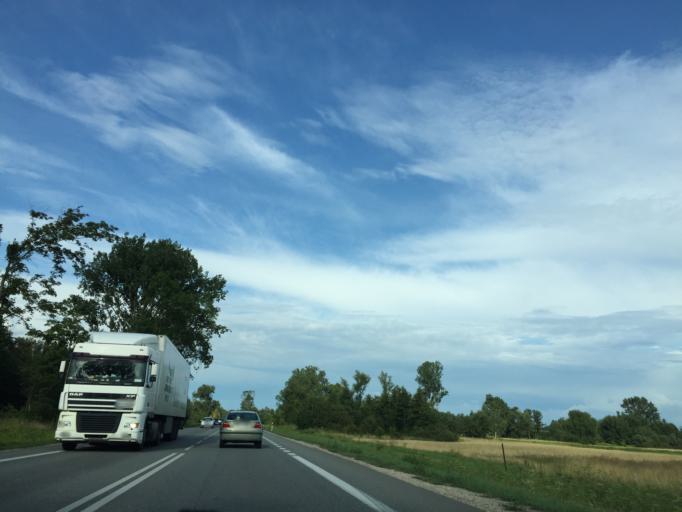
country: PL
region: Masovian Voivodeship
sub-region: Powiat piaseczynski
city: Gora Kalwaria
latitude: 52.0081
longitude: 21.2648
